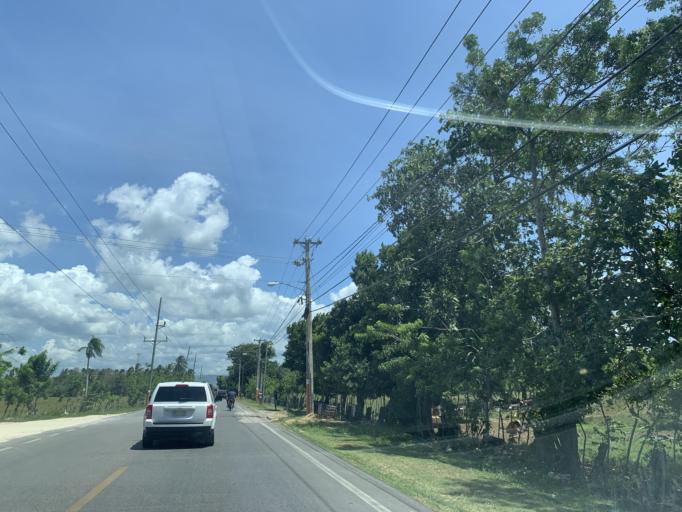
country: DO
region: Puerto Plata
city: Cabarete
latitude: 19.7255
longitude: -70.3875
